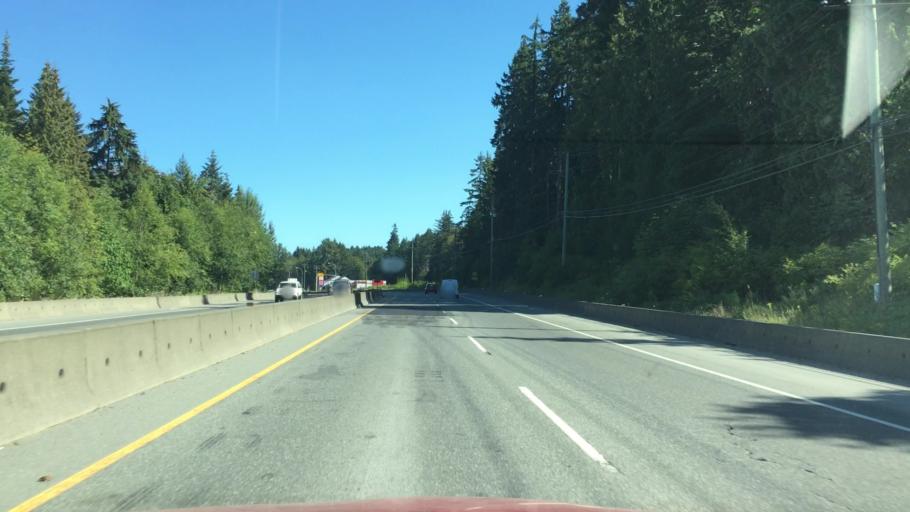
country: CA
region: British Columbia
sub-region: Cowichan Valley Regional District
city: Ladysmith
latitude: 49.0185
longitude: -123.8586
